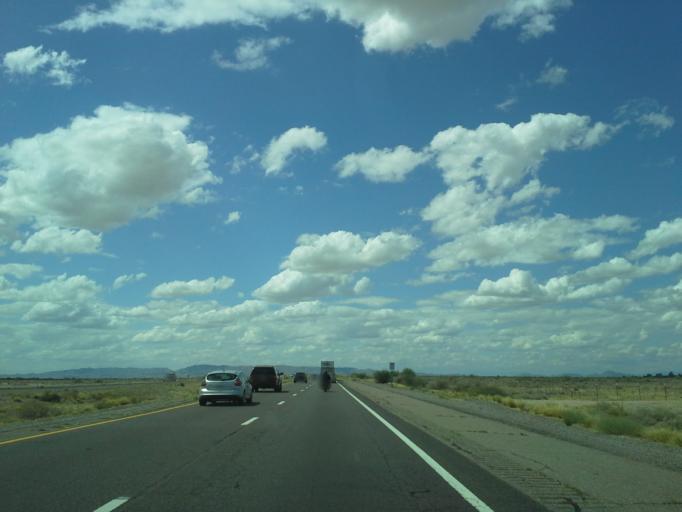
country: US
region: Arizona
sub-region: Maricopa County
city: Sun Lakes
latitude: 33.1760
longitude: -111.8865
